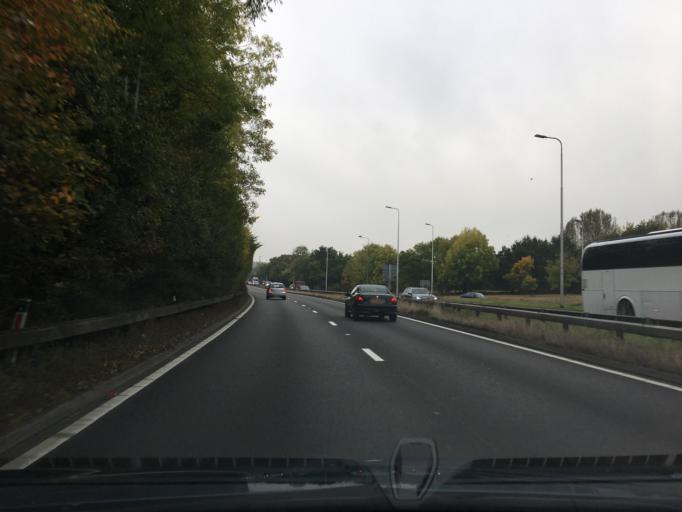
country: GB
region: England
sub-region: Surrey
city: Guildford
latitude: 51.2397
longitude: -0.6003
